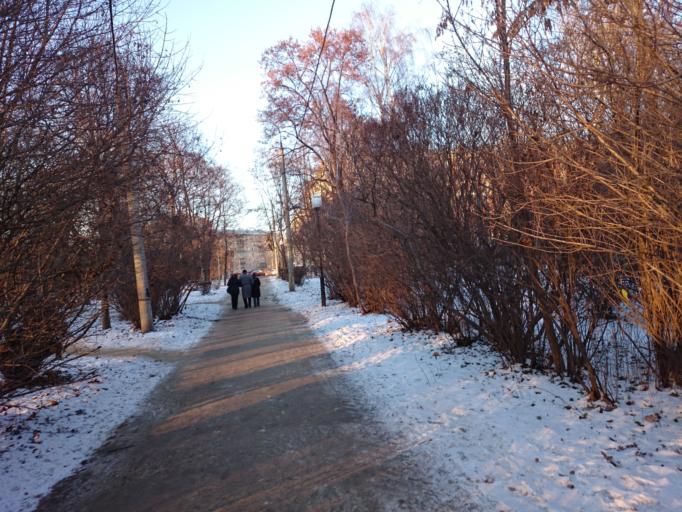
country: RU
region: Moscow
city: Sokol
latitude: 55.7913
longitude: 37.5120
